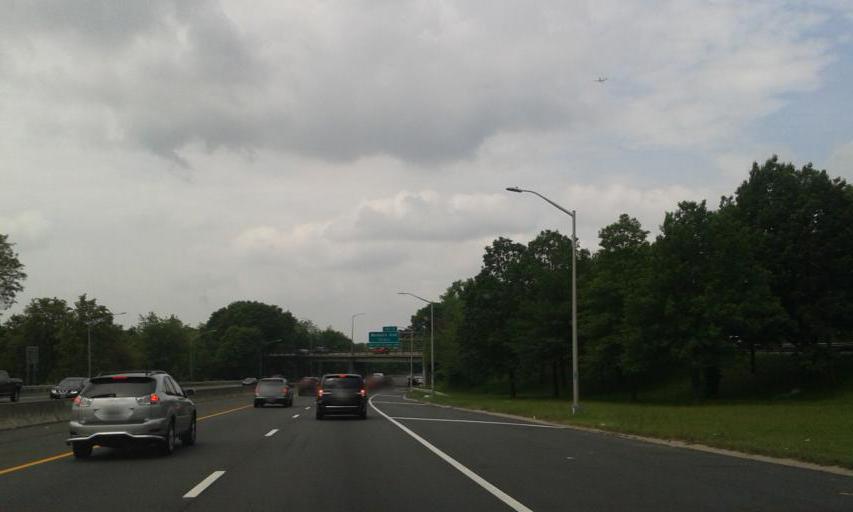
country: US
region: New York
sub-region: Richmond County
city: Bloomfield
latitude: 40.6216
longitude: -74.1711
